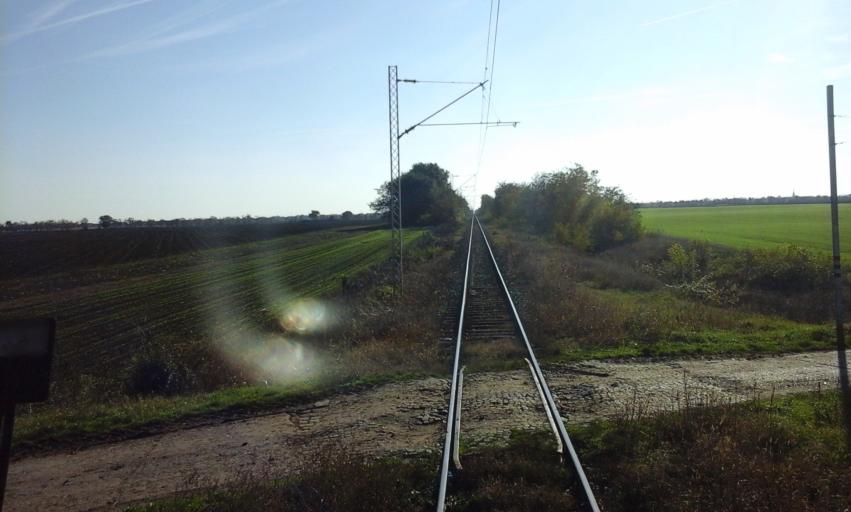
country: RS
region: Autonomna Pokrajina Vojvodina
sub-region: Severnobacki Okrug
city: Backa Topola
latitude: 45.8503
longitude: 19.6545
